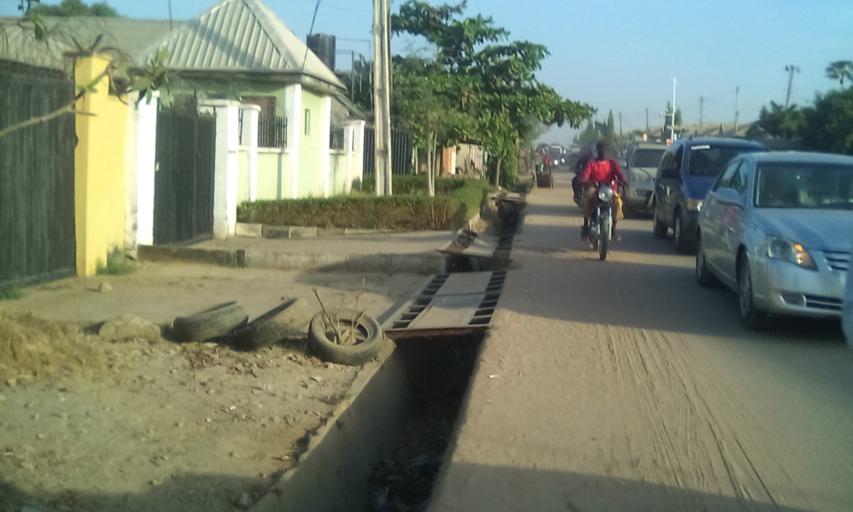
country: NG
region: Abuja Federal Capital Territory
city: Abuja
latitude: 8.9887
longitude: 7.3555
